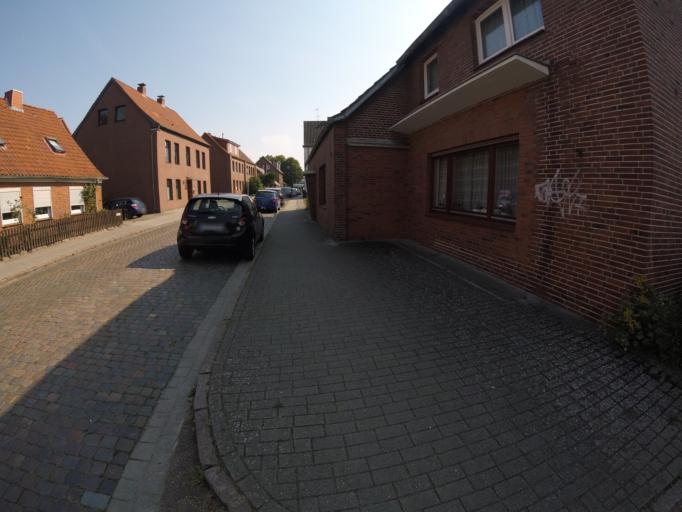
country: DE
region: Lower Saxony
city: Stade
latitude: 53.6072
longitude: 9.4752
